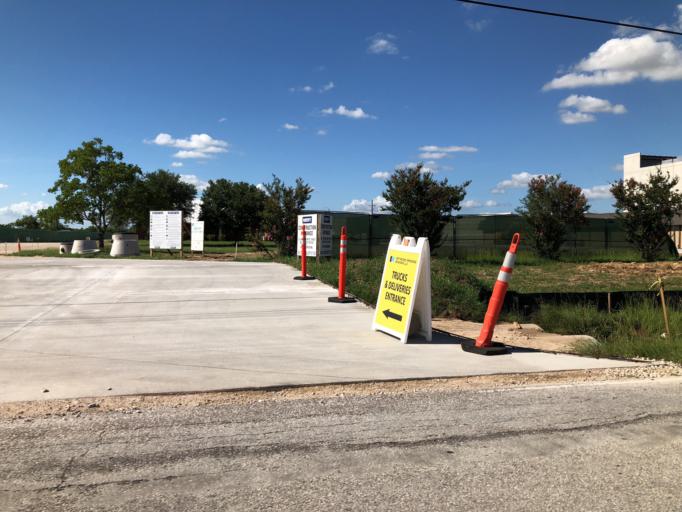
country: US
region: Texas
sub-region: Harris County
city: Katy
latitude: 29.8313
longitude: -95.8191
